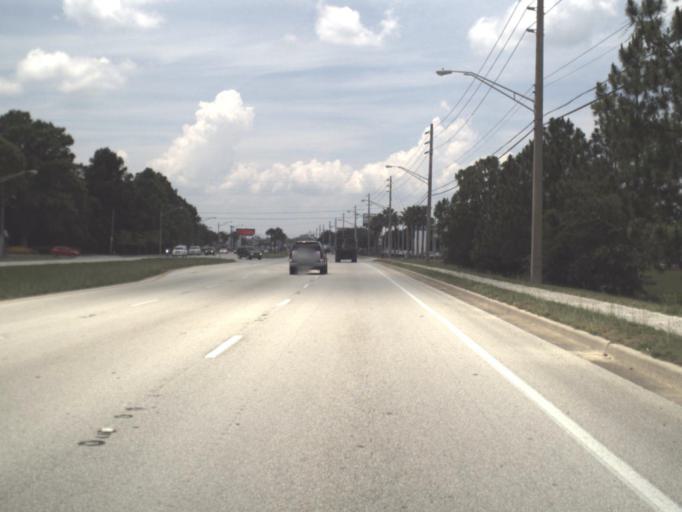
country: US
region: Florida
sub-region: Duval County
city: Atlantic Beach
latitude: 30.3246
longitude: -81.5106
